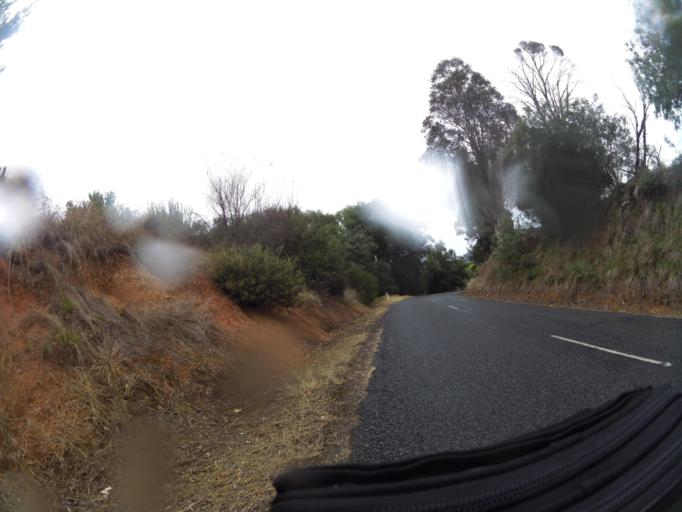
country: AU
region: New South Wales
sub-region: Greater Hume Shire
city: Holbrook
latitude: -36.2351
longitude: 147.6507
